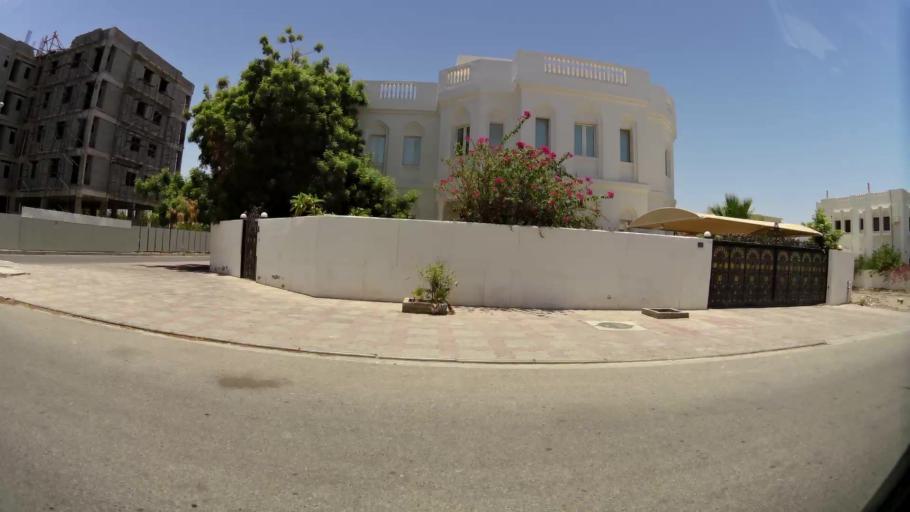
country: OM
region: Muhafazat Masqat
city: Bawshar
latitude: 23.6024
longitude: 58.4064
